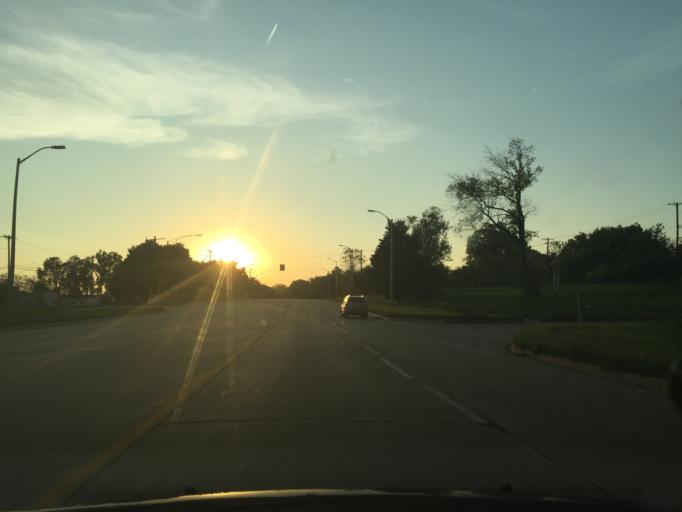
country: US
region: Michigan
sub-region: Oakland County
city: Pontiac
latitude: 42.6489
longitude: -83.2618
